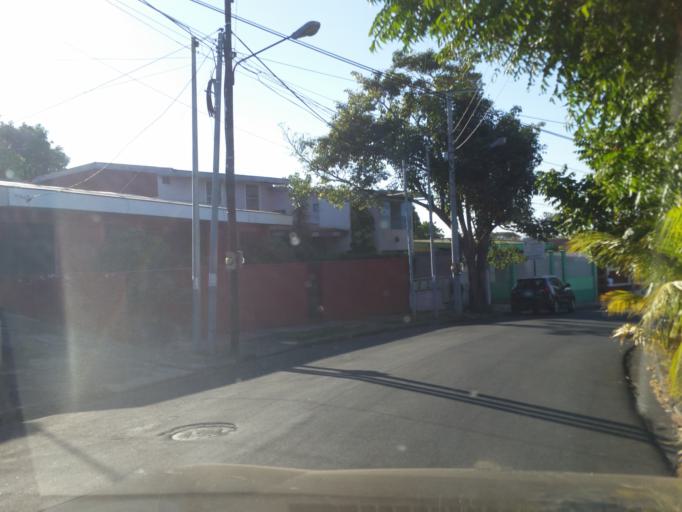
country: NI
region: Managua
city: Managua
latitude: 12.1414
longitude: -86.2778
